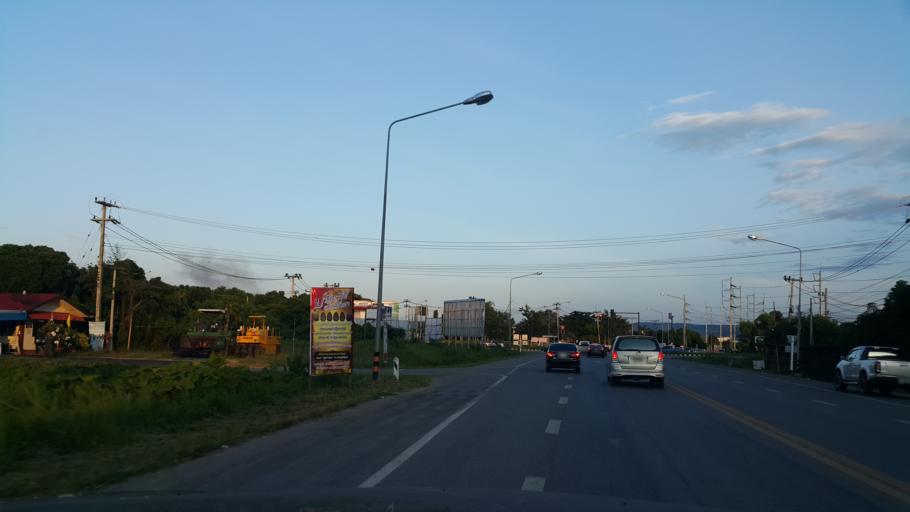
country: TH
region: Lamphun
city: Pa Sang
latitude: 18.4866
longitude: 98.9366
